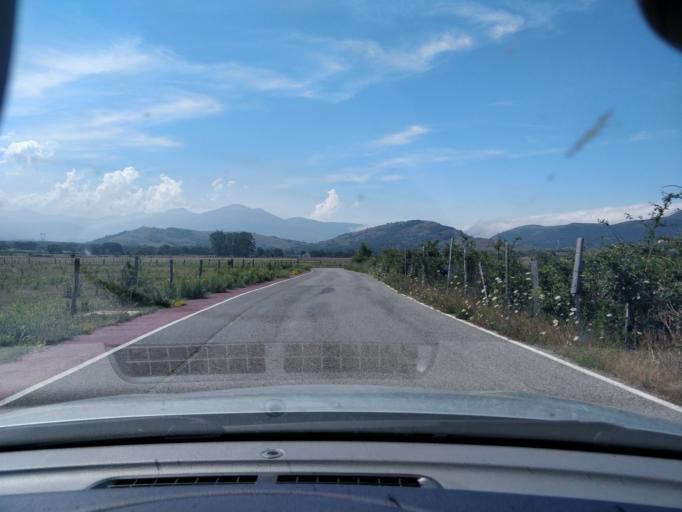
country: ES
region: Cantabria
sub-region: Provincia de Cantabria
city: Reinosa
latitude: 42.9924
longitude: -4.1604
